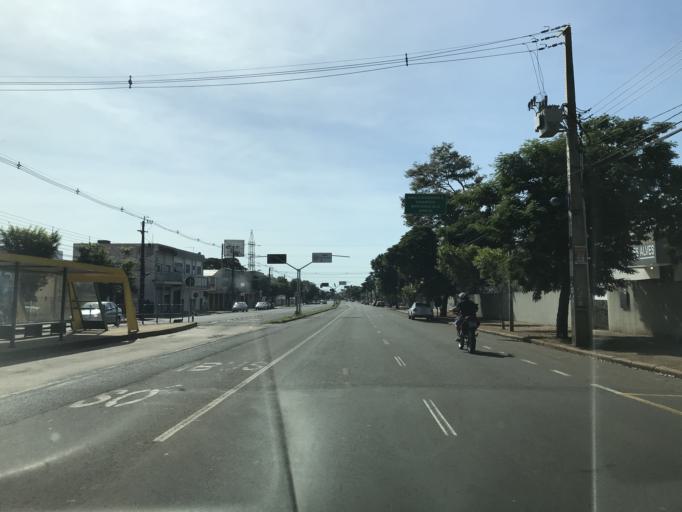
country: BR
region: Parana
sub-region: Maringa
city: Maringa
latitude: -23.4053
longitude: -51.9294
